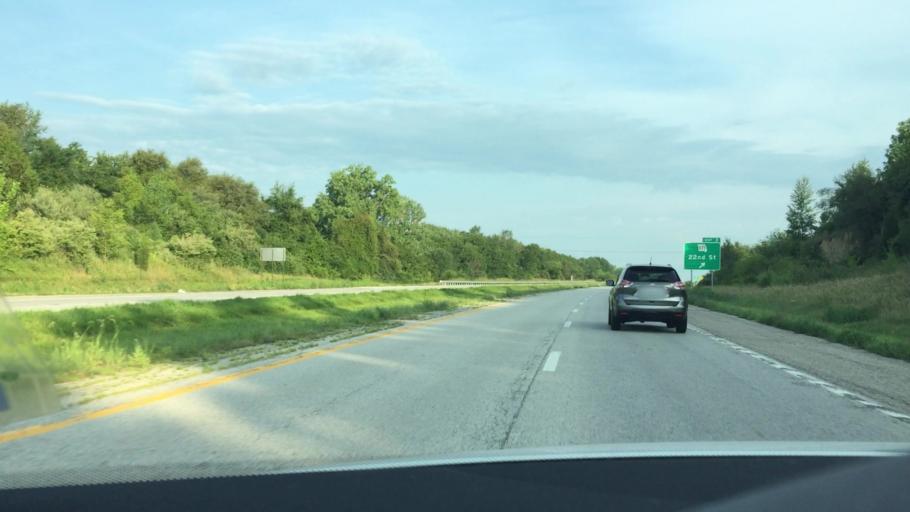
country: US
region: Missouri
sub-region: Buchanan County
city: Saint Joseph
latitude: 39.7188
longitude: -94.8271
